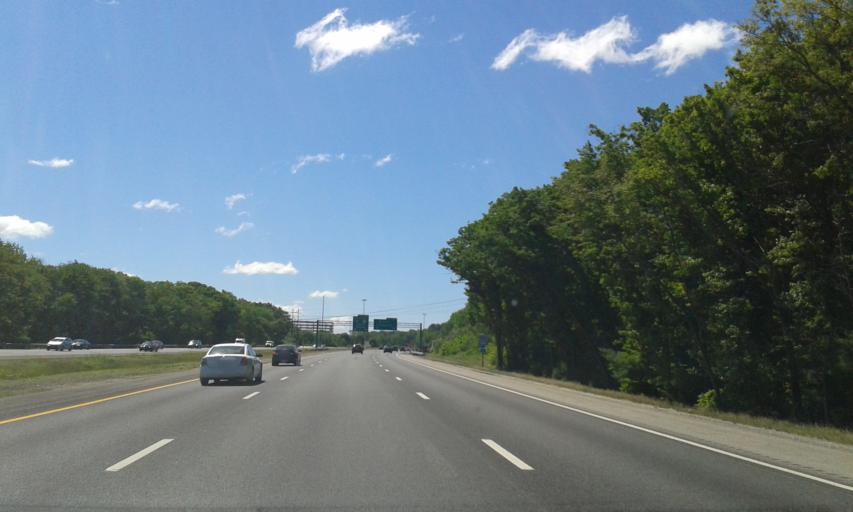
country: US
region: Massachusetts
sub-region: Middlesex County
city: Lexington
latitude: 42.4830
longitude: -71.2247
